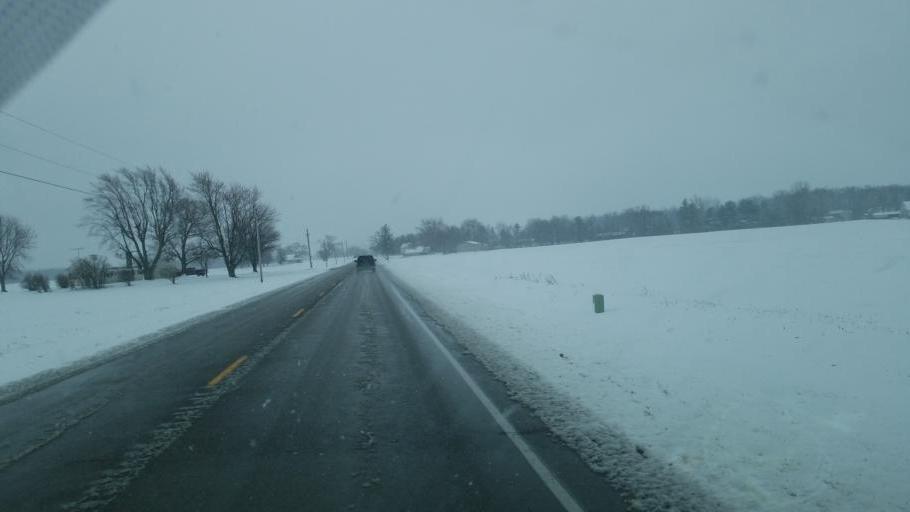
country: US
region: Indiana
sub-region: Delaware County
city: Muncie
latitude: 40.1032
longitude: -85.3175
